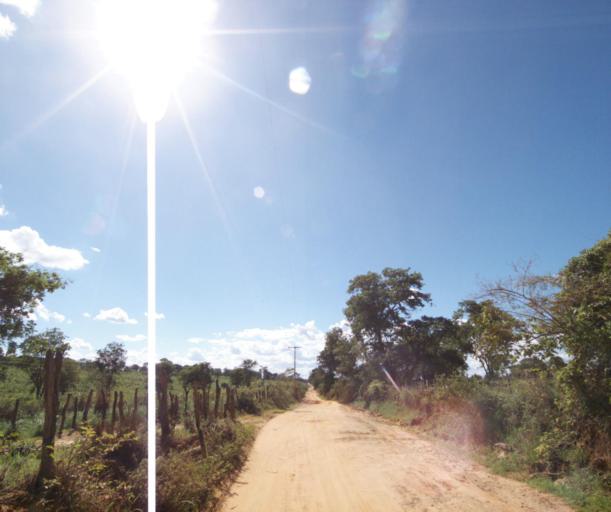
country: BR
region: Bahia
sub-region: Carinhanha
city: Carinhanha
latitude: -14.1834
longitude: -44.5038
